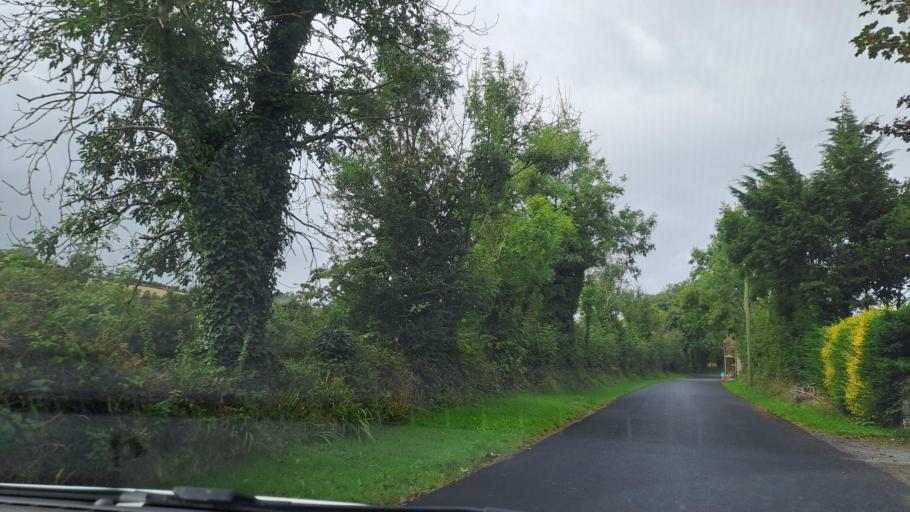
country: IE
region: Ulster
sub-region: County Monaghan
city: Carrickmacross
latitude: 53.9813
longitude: -6.7911
